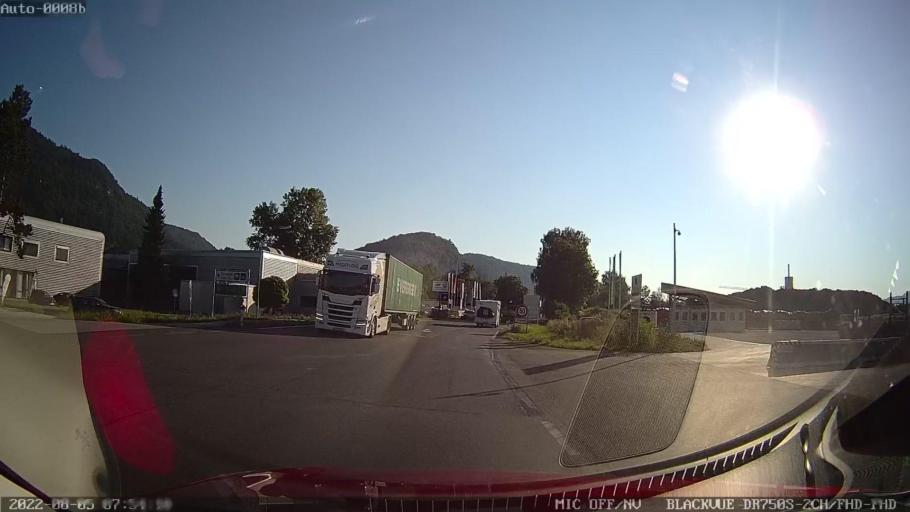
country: AT
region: Carinthia
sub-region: Politischer Bezirk Villach Land
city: Finkenstein am Faaker See
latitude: 46.5665
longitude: 13.8044
